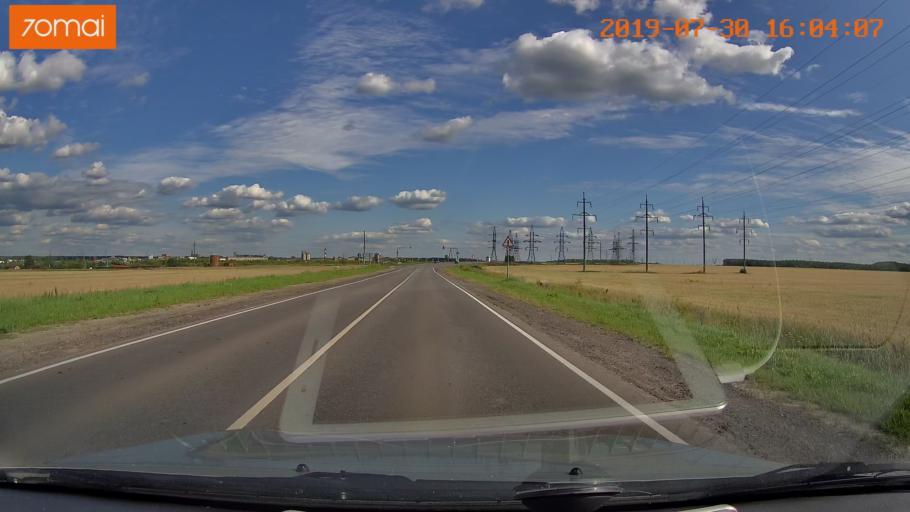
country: RU
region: Moskovskaya
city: Voskresensk
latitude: 55.2840
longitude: 38.7032
